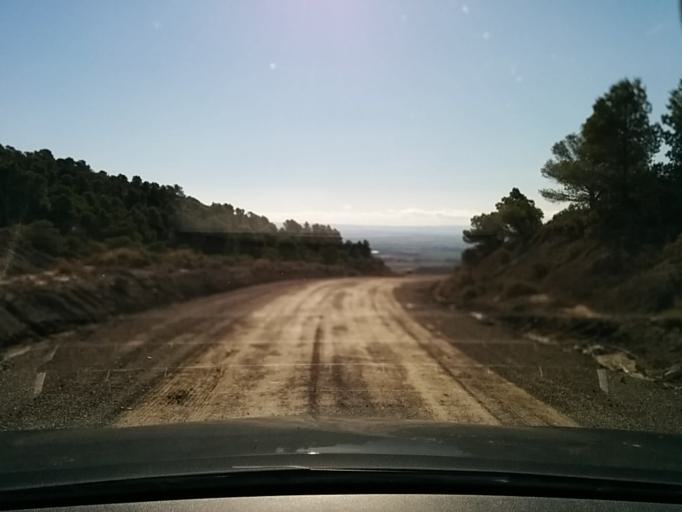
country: ES
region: Aragon
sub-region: Provincia de Zaragoza
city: Novillas
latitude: 42.0191
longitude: -1.3196
